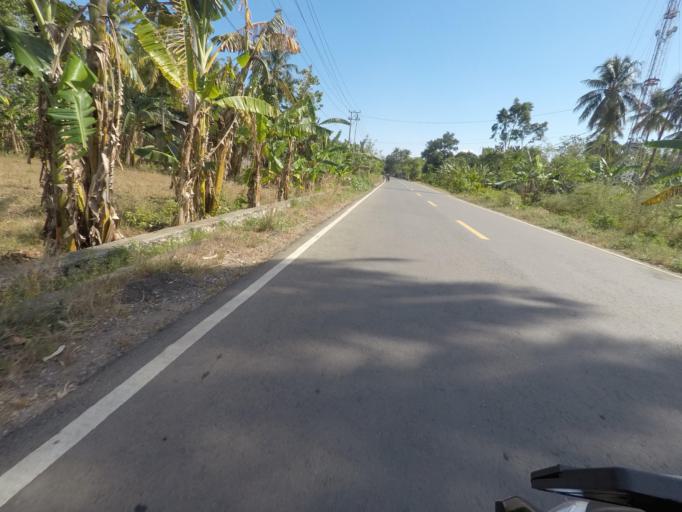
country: TL
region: Bobonaro
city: Maliana
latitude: -8.9629
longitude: 125.2161
